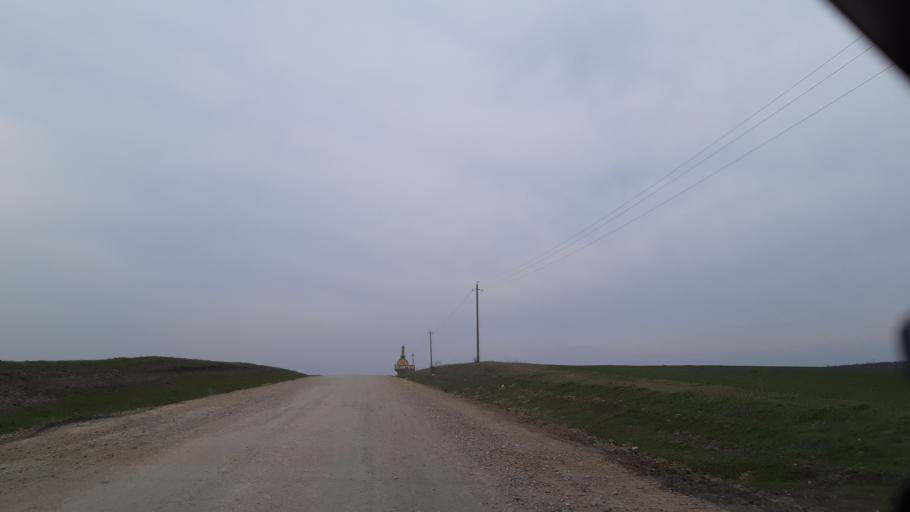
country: MD
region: Soldanesti
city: Soldanesti
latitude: 47.6220
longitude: 28.6584
